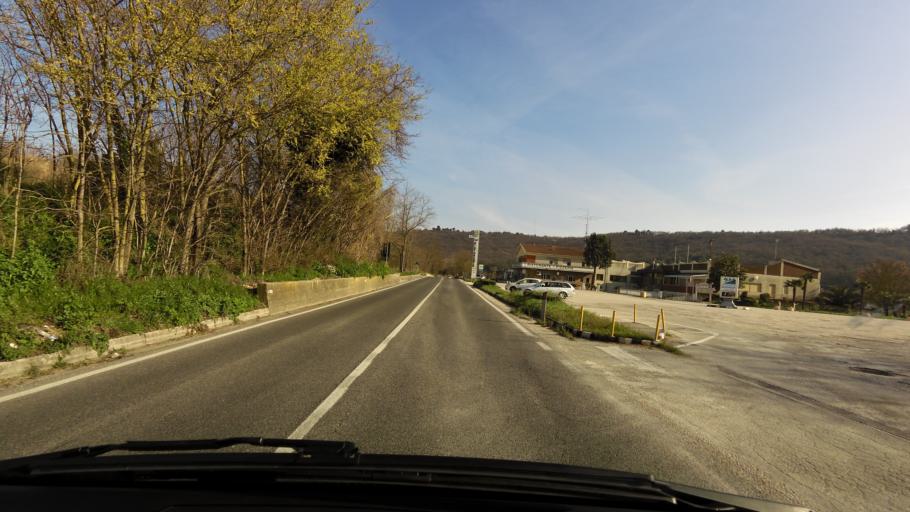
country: IT
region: The Marches
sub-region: Provincia di Ancona
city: Villa Musone
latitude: 43.4735
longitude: 13.5838
